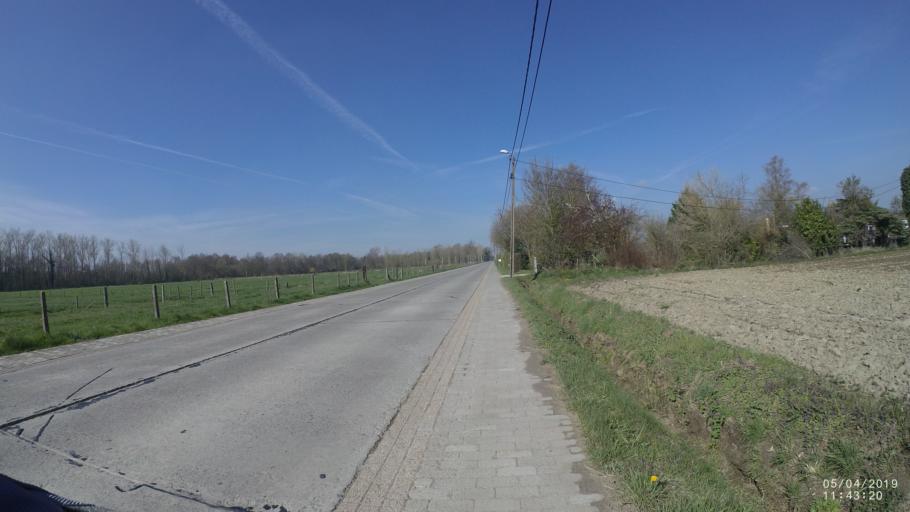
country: BE
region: Flanders
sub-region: Provincie Vlaams-Brabant
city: Geetbets
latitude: 50.8982
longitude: 5.1402
